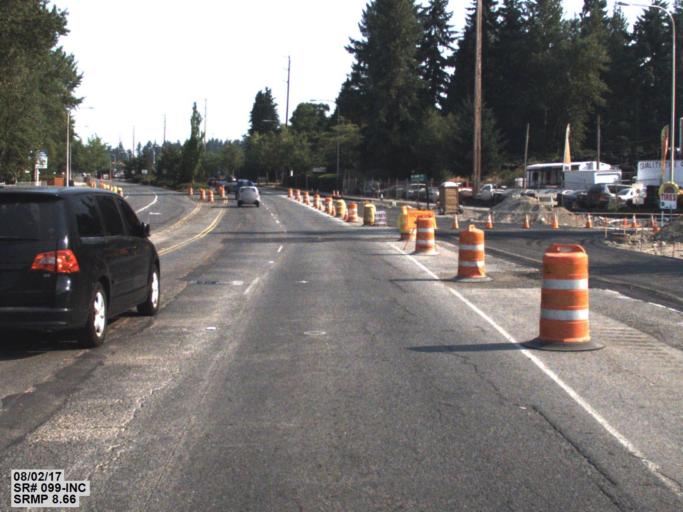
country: US
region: Washington
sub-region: King County
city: Federal Way
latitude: 47.2967
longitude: -122.3138
